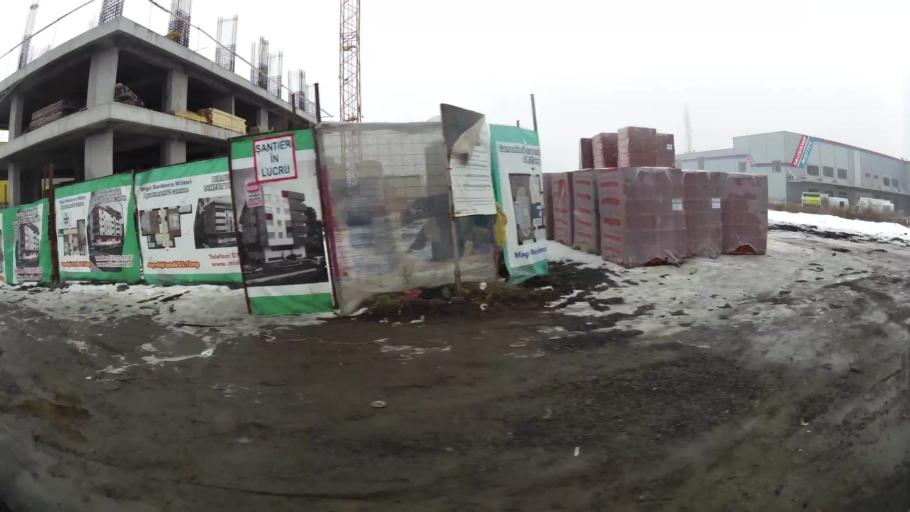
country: RO
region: Ilfov
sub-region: Comuna Chiajna
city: Chiajna
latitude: 44.4397
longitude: 25.9873
